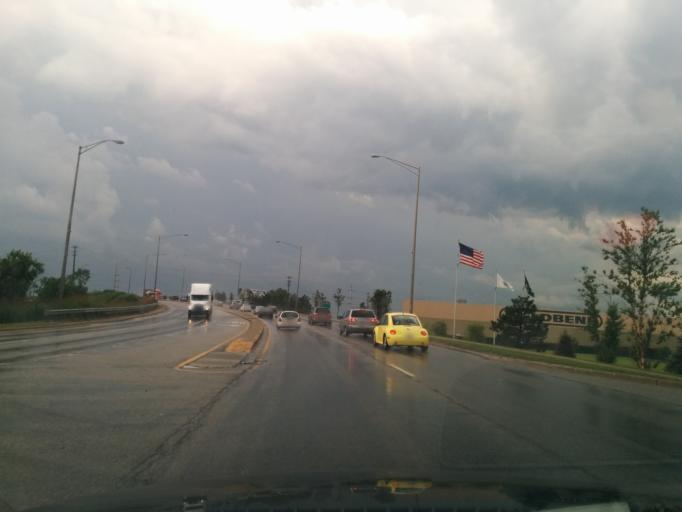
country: US
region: Illinois
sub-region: Cook County
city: Summit
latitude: 41.7723
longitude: -87.8044
